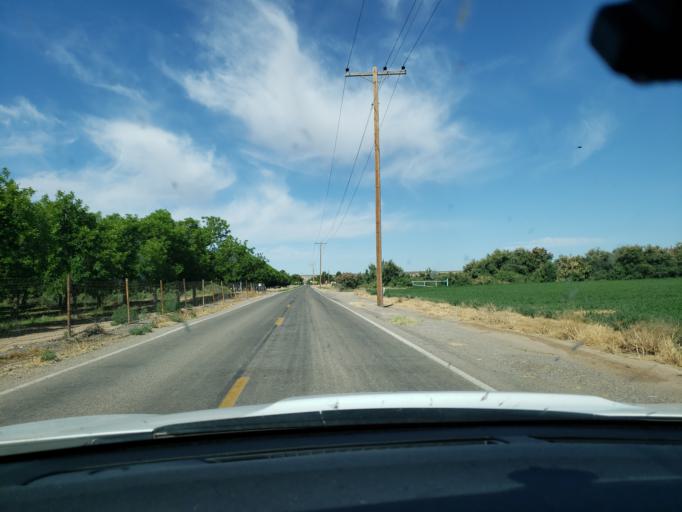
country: US
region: New Mexico
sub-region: Dona Ana County
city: Vado
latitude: 32.0628
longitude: -106.6728
